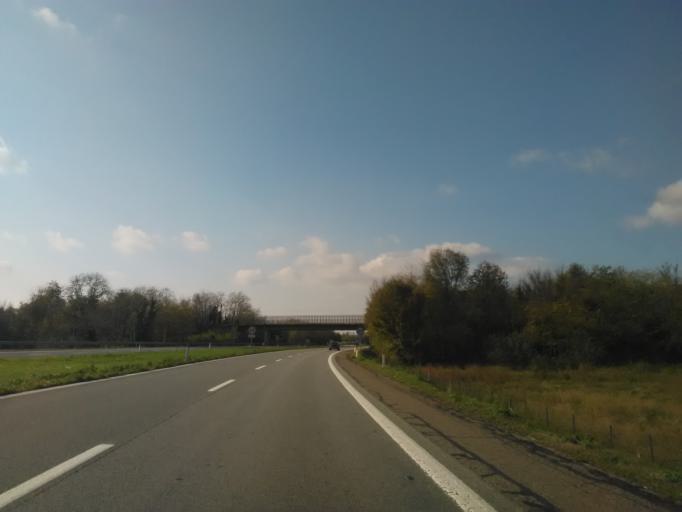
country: IT
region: Piedmont
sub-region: Provincia di Biella
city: Cavaglia
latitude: 45.3717
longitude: 8.1169
